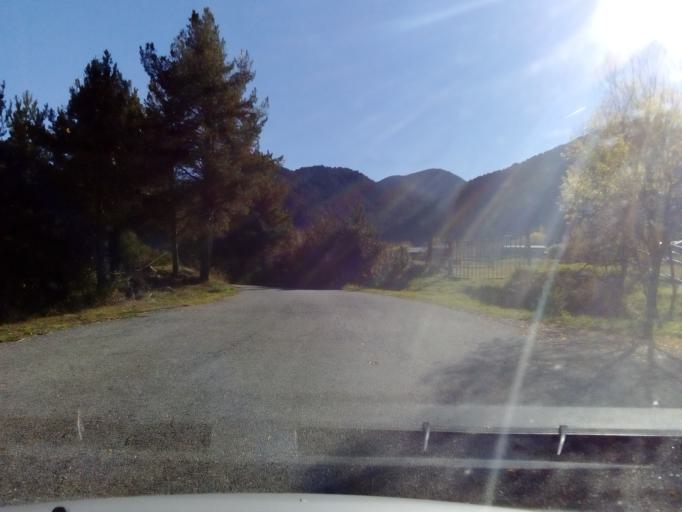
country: ES
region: Catalonia
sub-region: Provincia de Lleida
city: Bellver de Cerdanya
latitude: 42.3443
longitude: 1.7772
